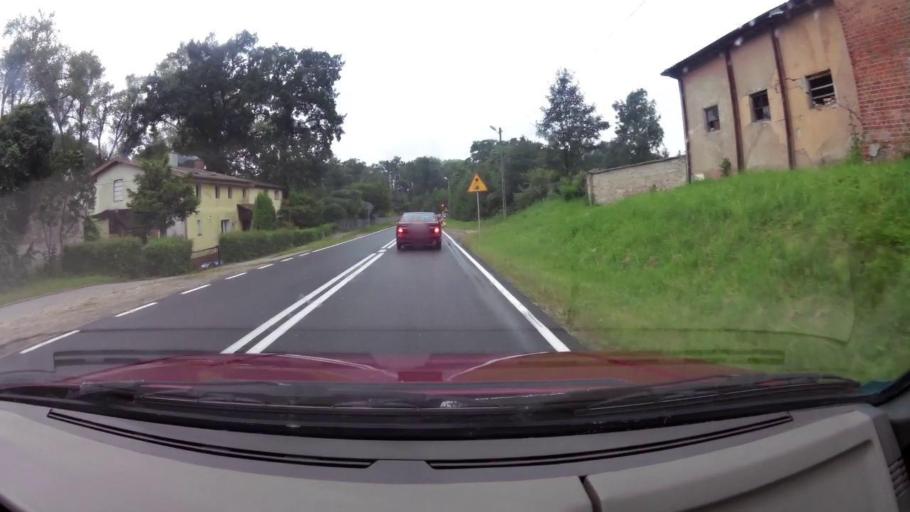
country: PL
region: West Pomeranian Voivodeship
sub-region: Powiat stargardzki
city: Marianowo
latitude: 53.4143
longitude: 15.2392
